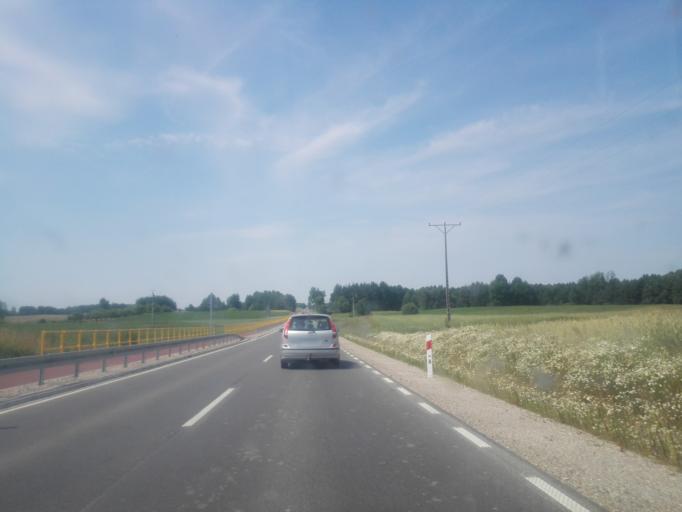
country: PL
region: Podlasie
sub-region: Powiat sejnenski
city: Sejny
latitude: 54.1086
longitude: 23.2762
